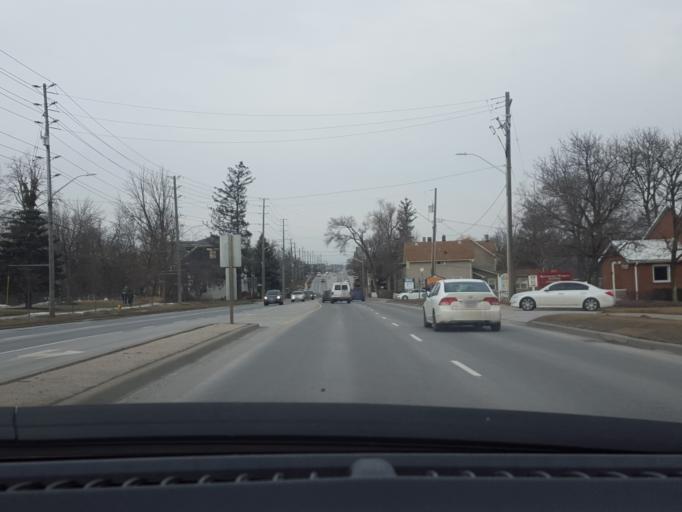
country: CA
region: Ontario
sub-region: York
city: Richmond Hill
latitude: 43.8594
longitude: -79.3605
